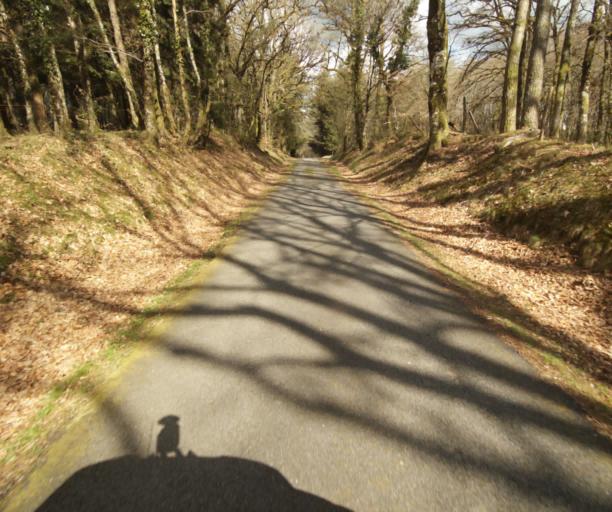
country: FR
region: Limousin
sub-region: Departement de la Correze
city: Argentat
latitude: 45.2268
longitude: 1.9300
